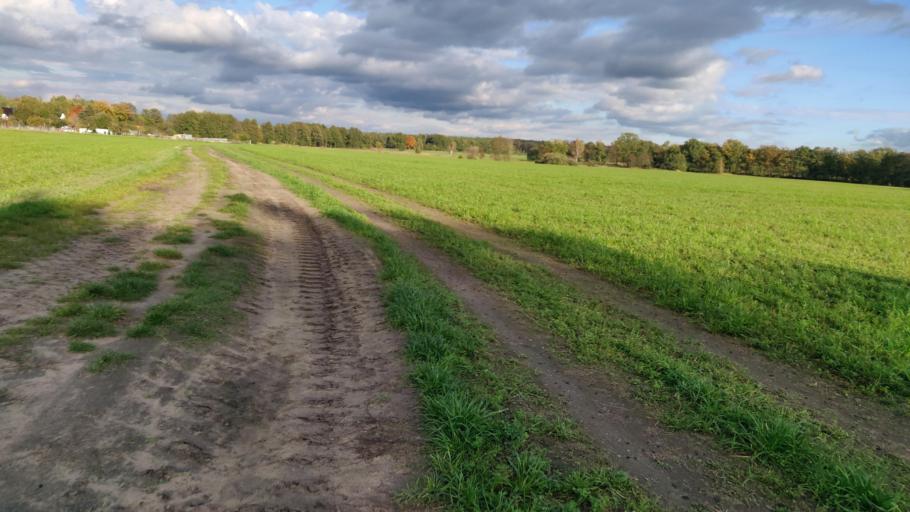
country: DE
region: Brandenburg
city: Ortrand
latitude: 51.3666
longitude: 13.7722
